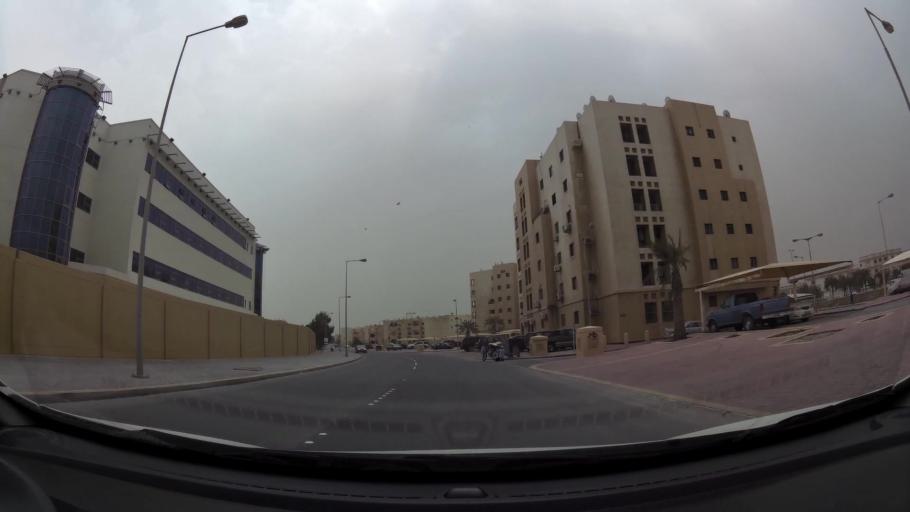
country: BH
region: Northern
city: Madinat `Isa
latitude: 26.1815
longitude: 50.5386
